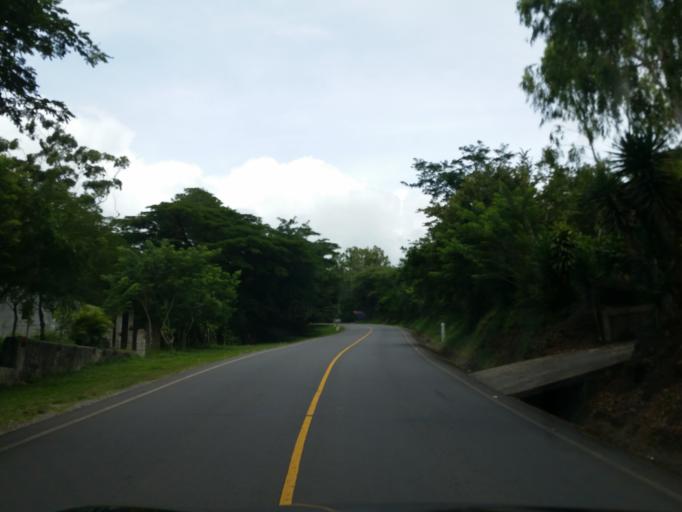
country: NI
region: Matagalpa
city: Matagalpa
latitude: 12.9567
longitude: -85.9203
